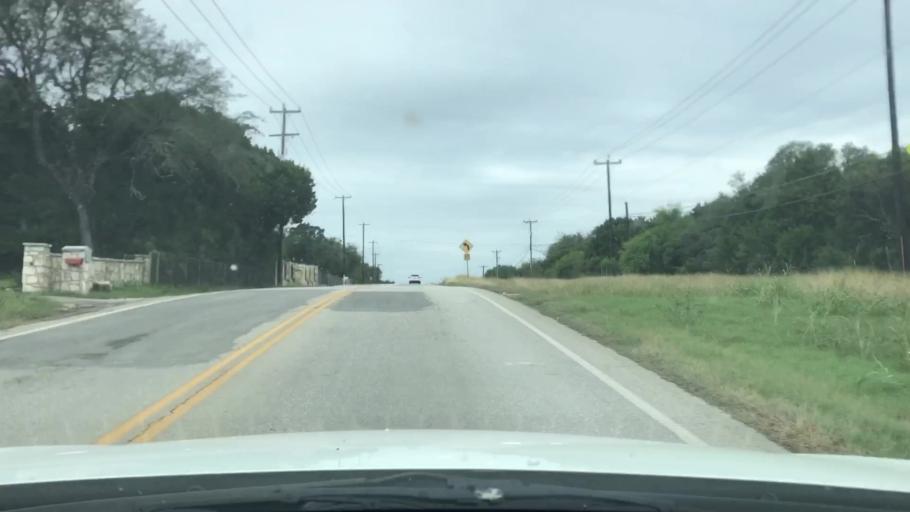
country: US
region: Texas
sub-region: Bexar County
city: Timberwood Park
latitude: 29.6469
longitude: -98.4075
